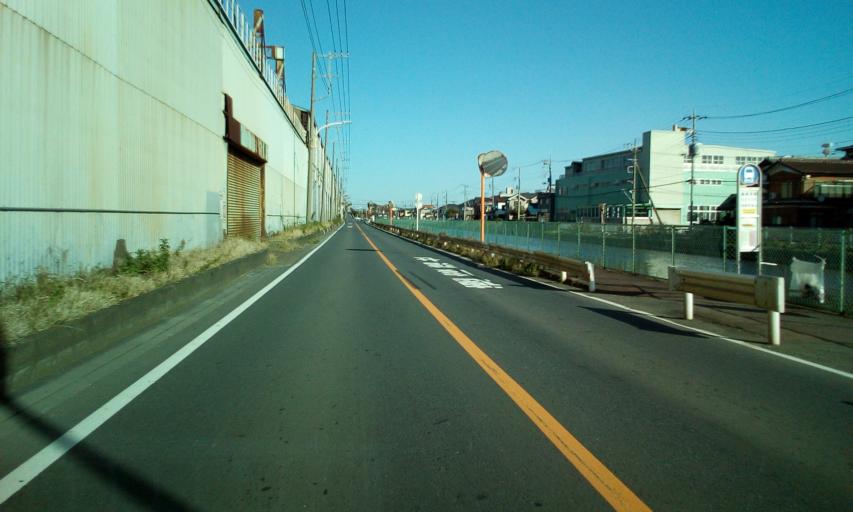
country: JP
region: Chiba
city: Matsudo
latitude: 35.8131
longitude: 139.8837
